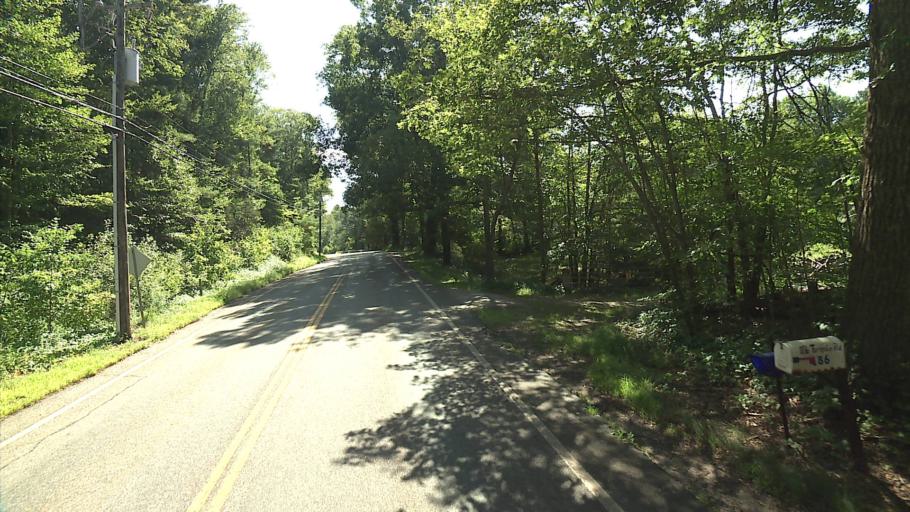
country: US
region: Connecticut
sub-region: Tolland County
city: Stafford Springs
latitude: 41.9168
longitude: -72.1897
